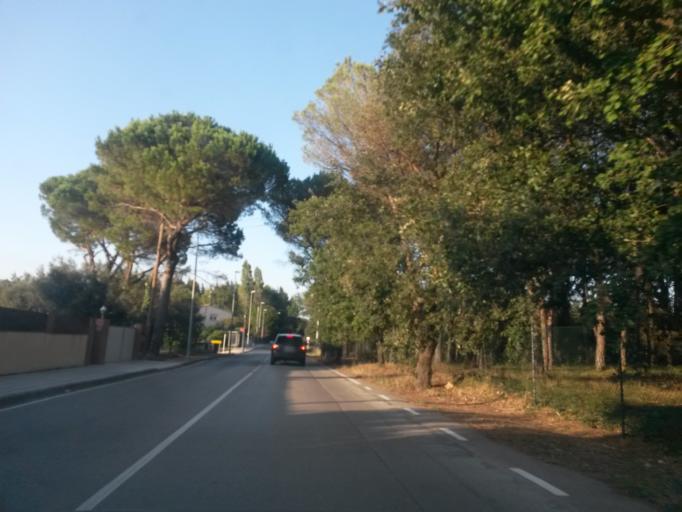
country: ES
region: Catalonia
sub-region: Provincia de Girona
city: Fornells de la Selva
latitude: 41.9418
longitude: 2.8094
